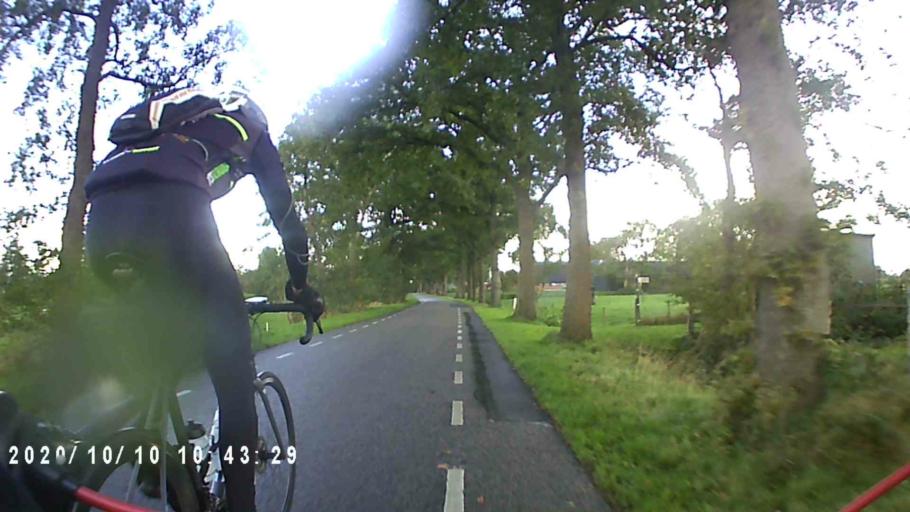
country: NL
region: Groningen
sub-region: Gemeente Grootegast
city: Grootegast
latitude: 53.1728
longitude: 6.2676
